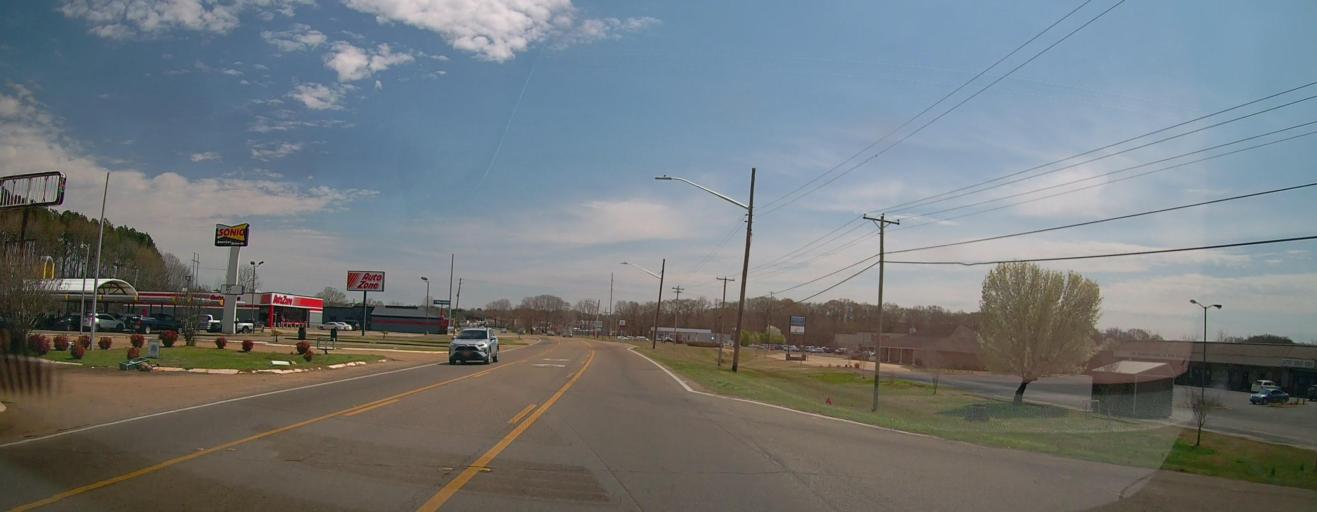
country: US
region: Mississippi
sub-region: Union County
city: New Albany
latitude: 34.4963
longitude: -89.0197
